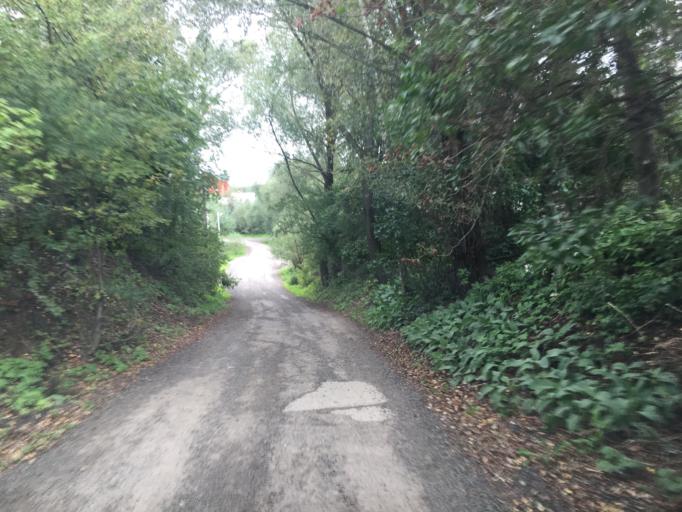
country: RU
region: Moskovskaya
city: Dubrovitsy
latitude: 55.4756
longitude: 37.4176
